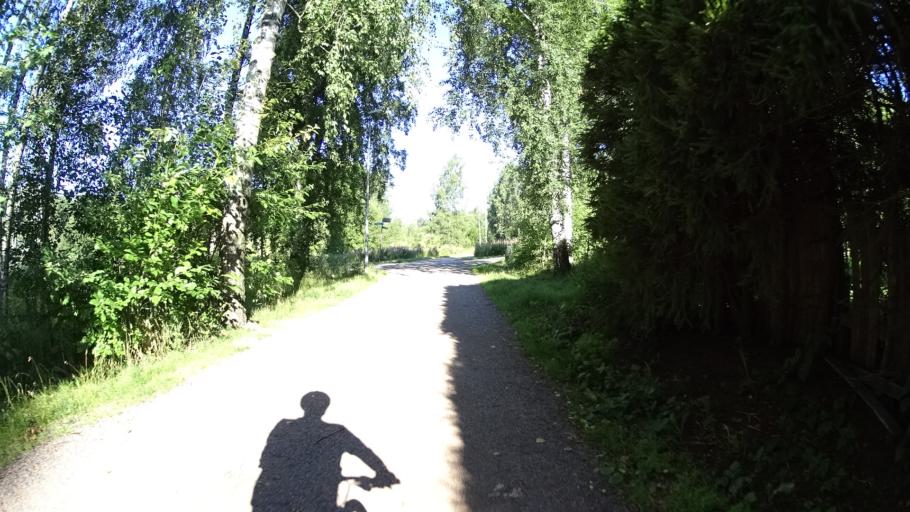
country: FI
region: Uusimaa
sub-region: Helsinki
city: Teekkarikylae
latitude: 60.2509
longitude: 24.8766
